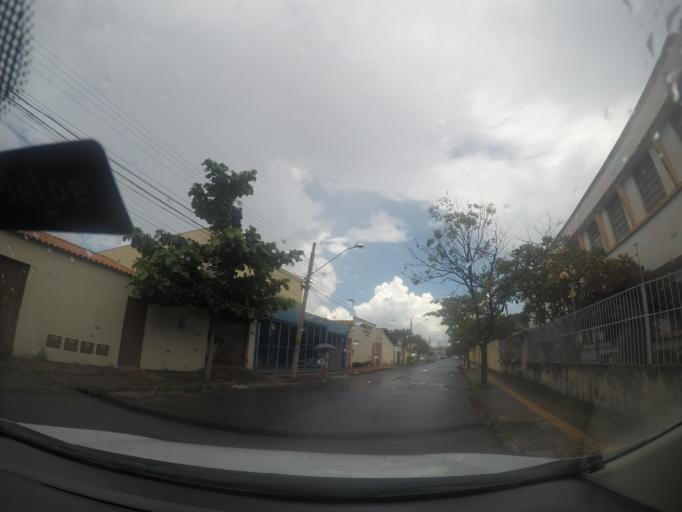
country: BR
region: Goias
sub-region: Goiania
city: Goiania
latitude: -16.6782
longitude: -49.2872
